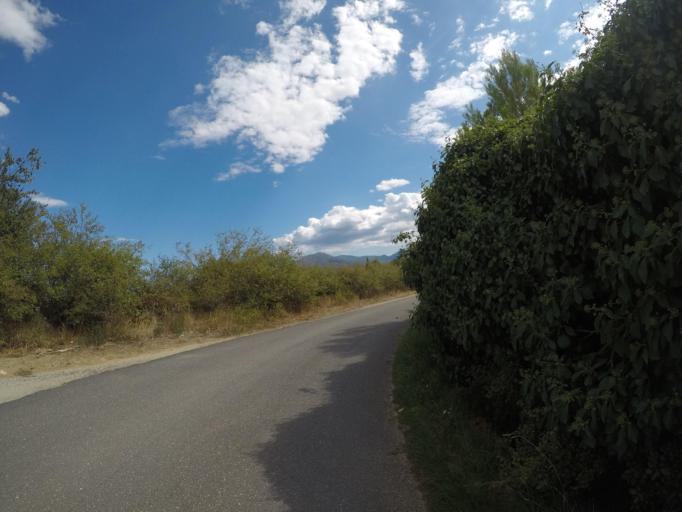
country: FR
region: Languedoc-Roussillon
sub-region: Departement des Pyrenees-Orientales
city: Sant Joan de Pladecorts
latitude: 42.5141
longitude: 2.7816
